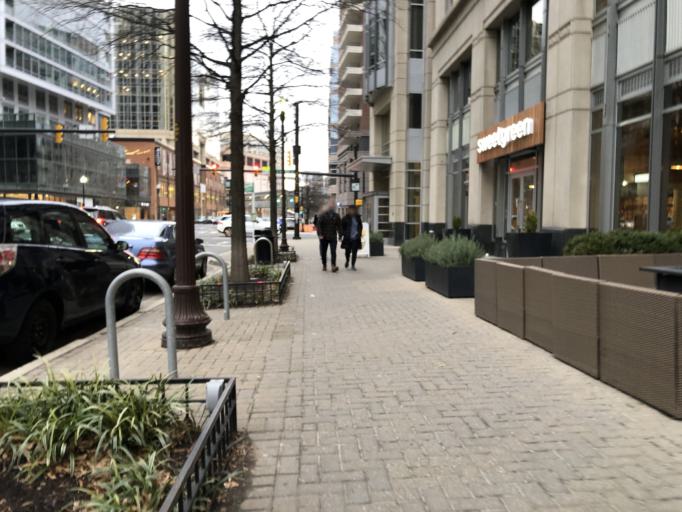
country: US
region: Virginia
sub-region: Arlington County
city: Arlington
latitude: 38.8800
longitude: -77.1085
